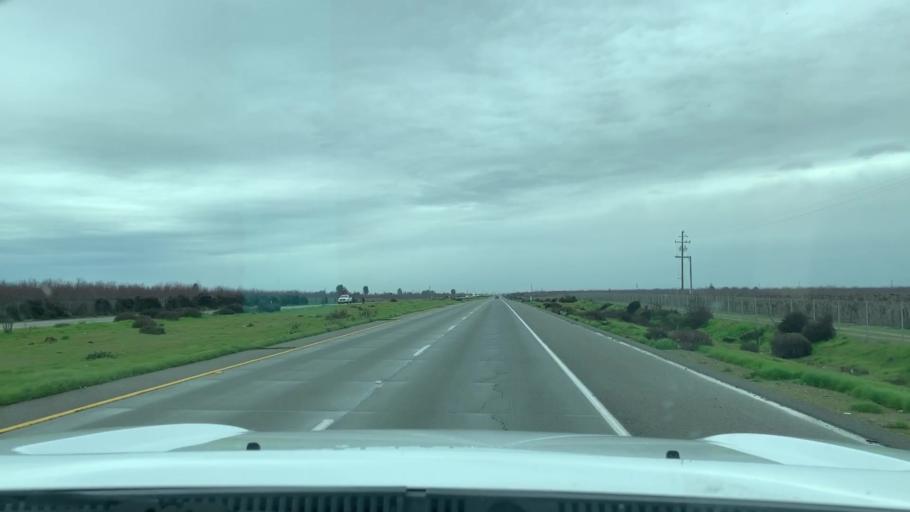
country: US
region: California
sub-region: Fresno County
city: Caruthers
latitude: 36.5300
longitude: -119.7860
